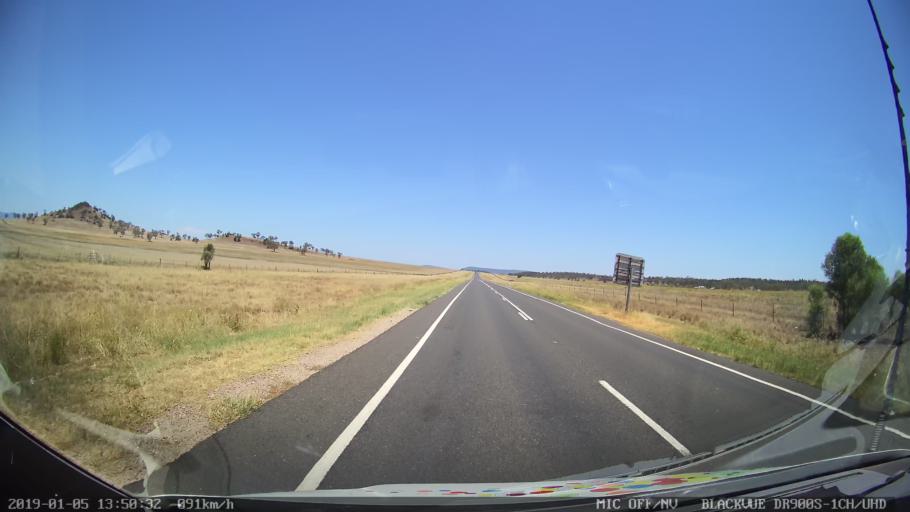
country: AU
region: New South Wales
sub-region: Gunnedah
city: Gunnedah
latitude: -31.0313
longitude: 150.2752
